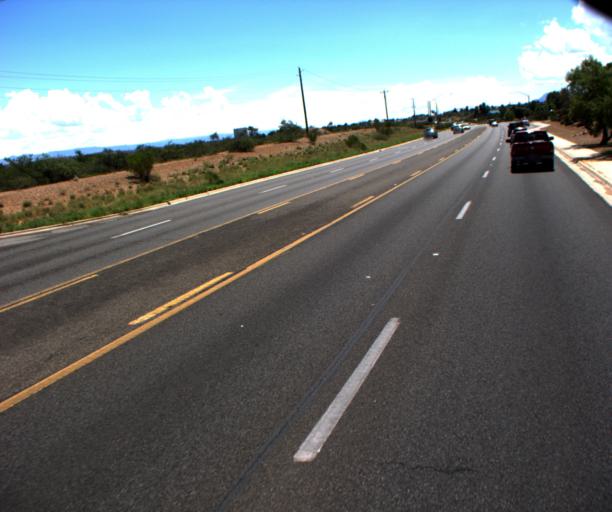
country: US
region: Arizona
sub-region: Yavapai County
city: Verde Village
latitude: 34.7165
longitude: -112.0006
